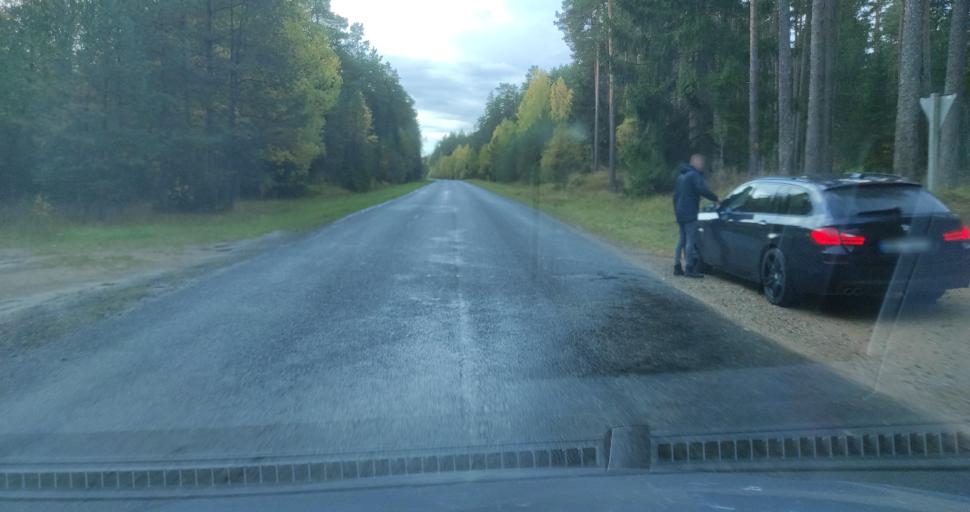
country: LV
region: Skrunda
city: Skrunda
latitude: 56.6450
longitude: 22.0105
